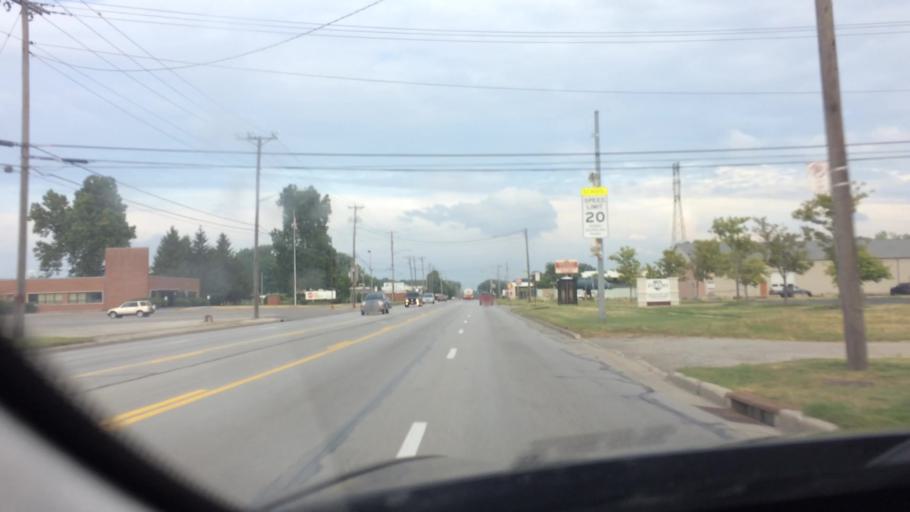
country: US
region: Ohio
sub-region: Lucas County
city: Ottawa Hills
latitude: 41.6380
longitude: -83.6143
